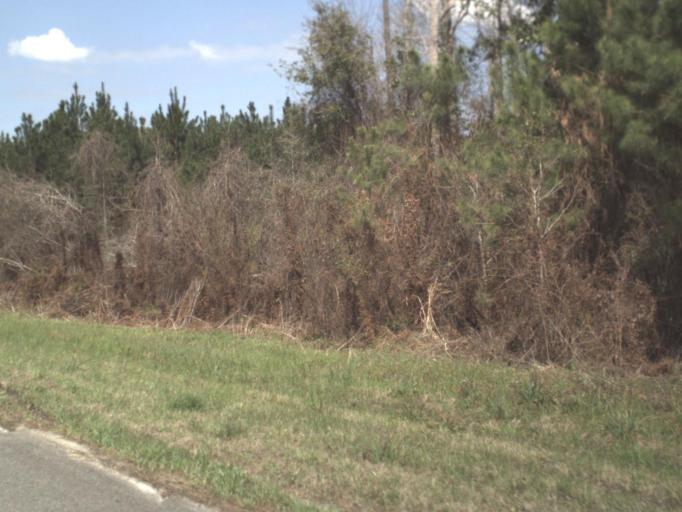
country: US
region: Florida
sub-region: Gadsden County
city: Quincy
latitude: 30.3880
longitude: -84.6809
